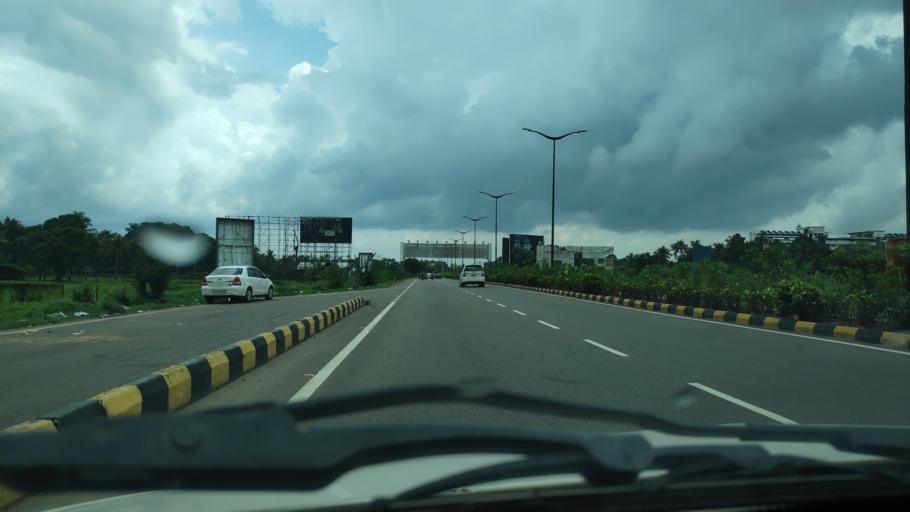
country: IN
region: Kerala
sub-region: Ernakulam
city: Aluva
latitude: 10.1500
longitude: 76.3611
